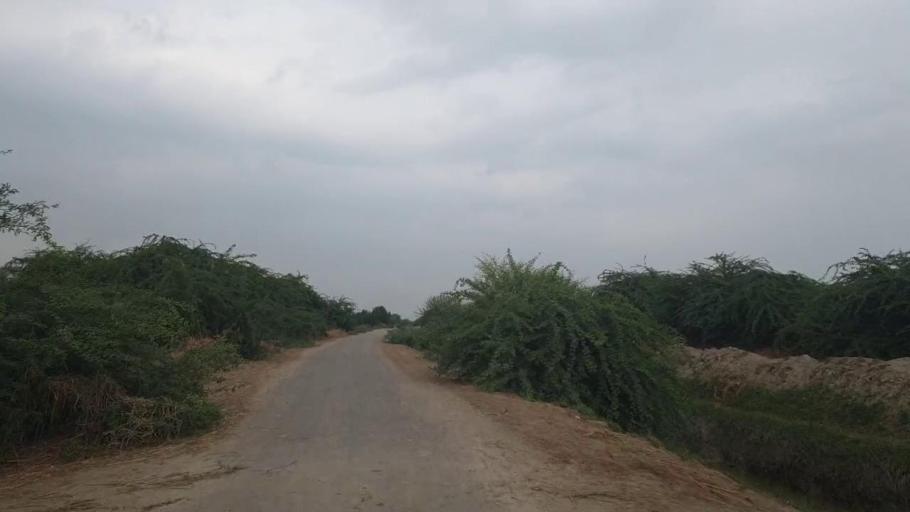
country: PK
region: Sindh
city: Badin
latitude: 24.6193
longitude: 68.6815
